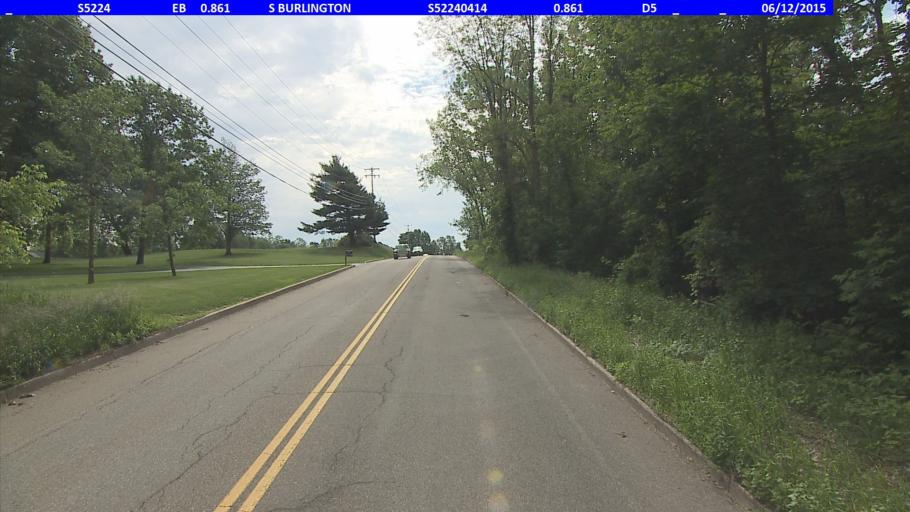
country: US
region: Vermont
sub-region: Chittenden County
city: South Burlington
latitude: 44.4442
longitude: -73.1921
